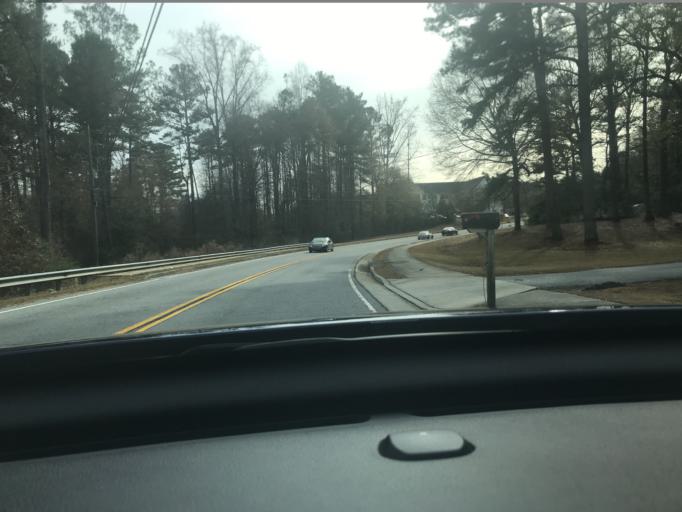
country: US
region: Georgia
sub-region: Gwinnett County
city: Mountain Park
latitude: 33.8730
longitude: -84.0902
